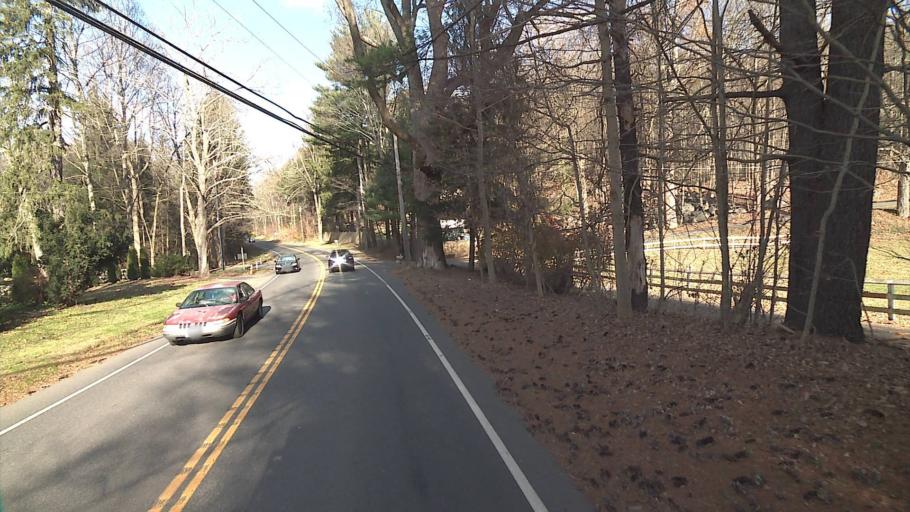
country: US
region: Connecticut
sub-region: Fairfield County
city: Bethel
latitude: 41.3461
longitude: -73.4144
